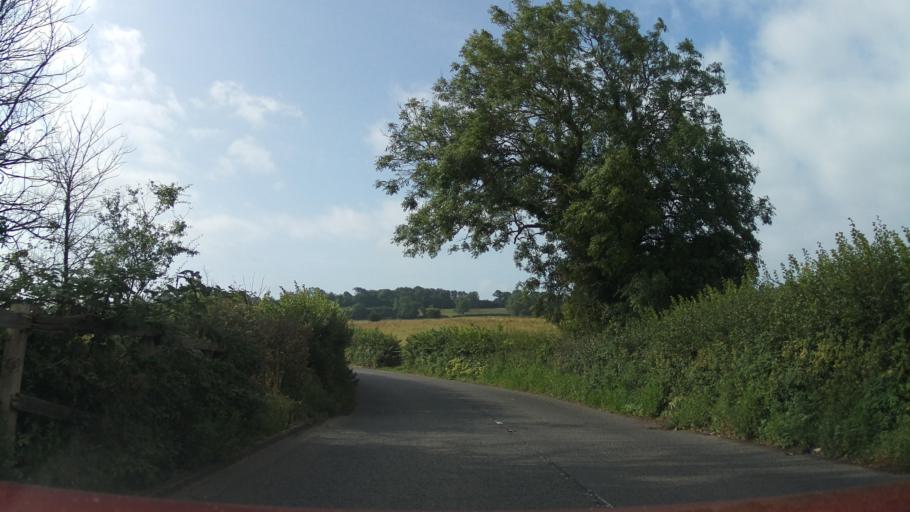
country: GB
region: England
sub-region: North Somerset
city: Winford
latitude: 51.3998
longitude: -2.6719
